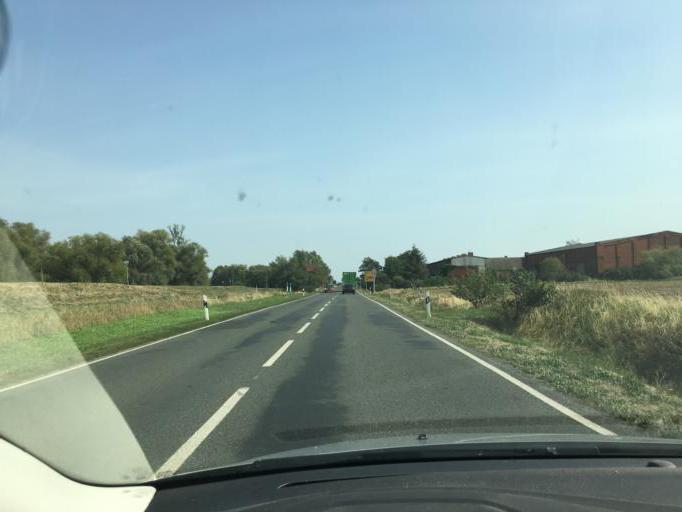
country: DE
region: Saxony-Anhalt
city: Plotzky
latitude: 52.0075
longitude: 11.7975
